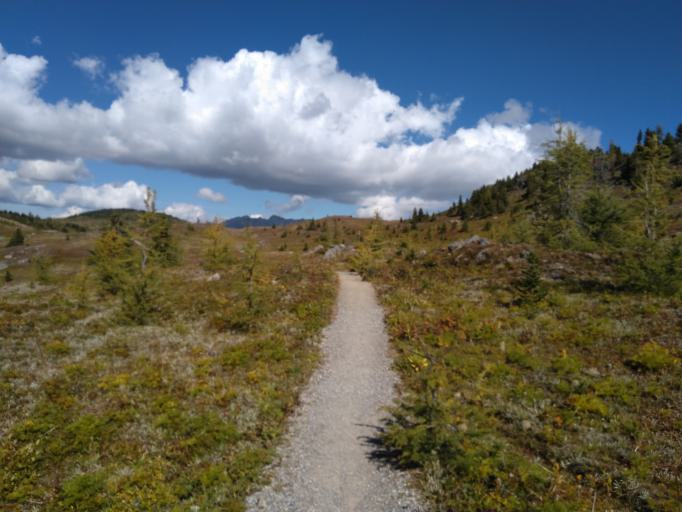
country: CA
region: Alberta
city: Banff
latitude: 51.0699
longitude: -115.7907
